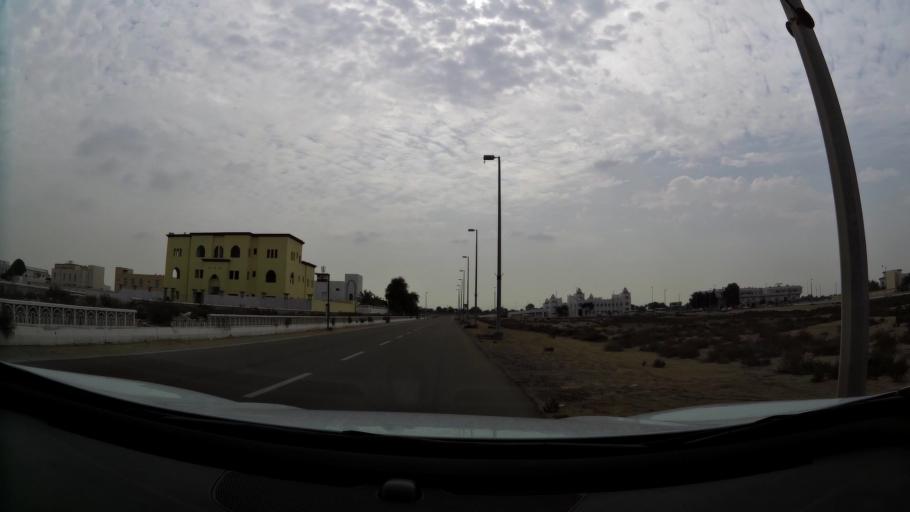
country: AE
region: Abu Dhabi
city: Abu Dhabi
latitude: 24.6393
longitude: 54.7265
